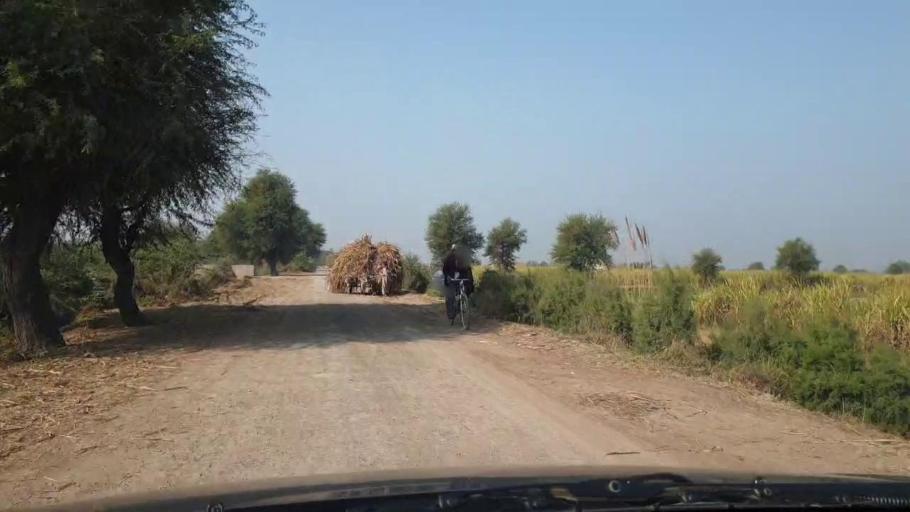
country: PK
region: Sindh
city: Jhol
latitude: 25.9602
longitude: 68.9338
